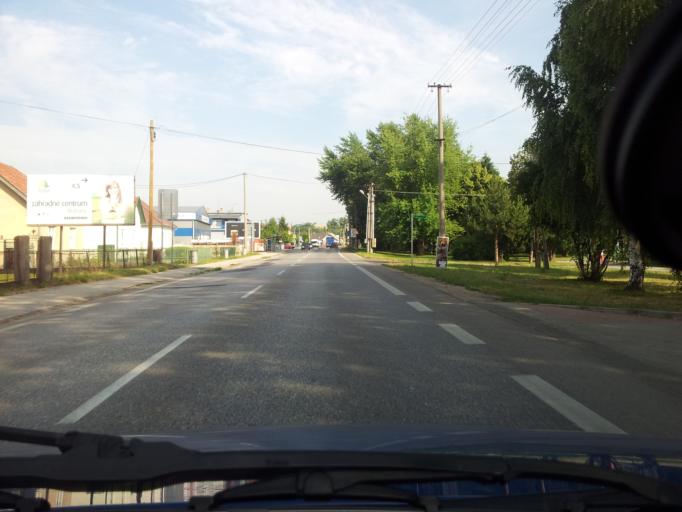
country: SK
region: Nitriansky
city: Partizanske
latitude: 48.6296
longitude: 18.3545
